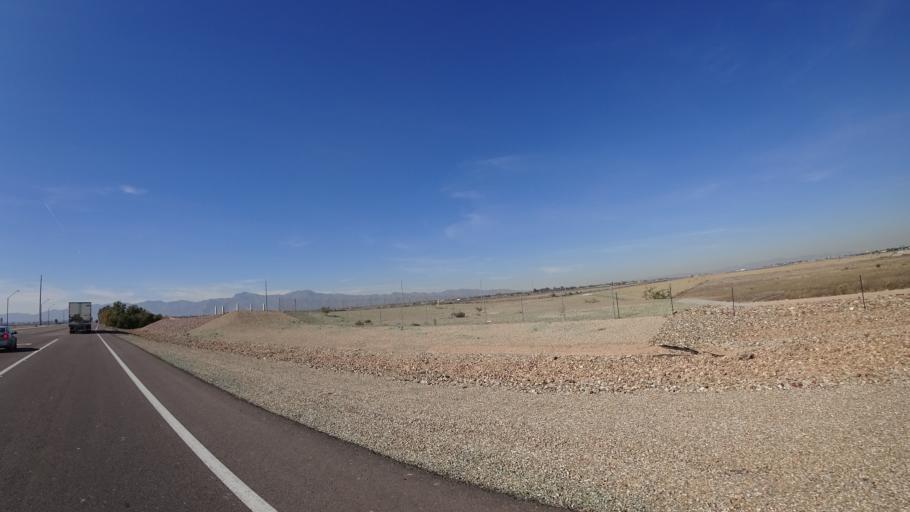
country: US
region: Arizona
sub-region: Maricopa County
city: Citrus Park
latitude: 33.5082
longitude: -112.4219
